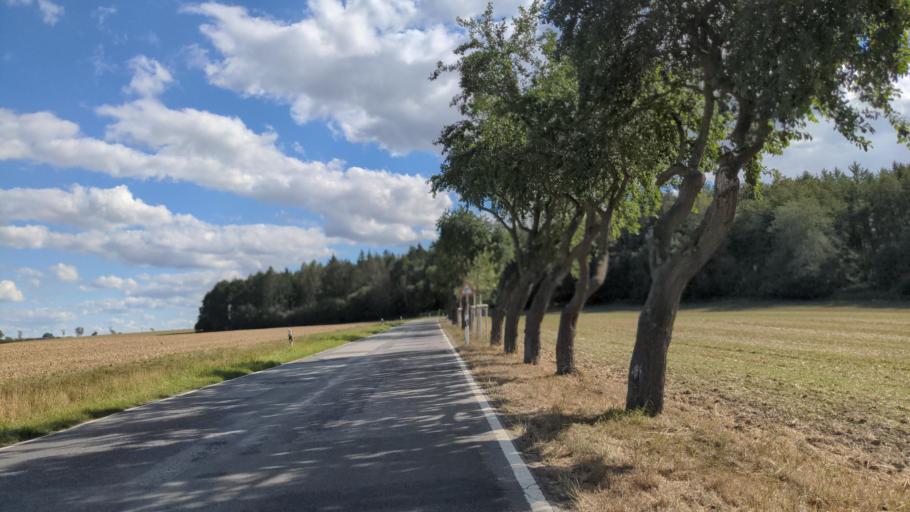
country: DE
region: Mecklenburg-Vorpommern
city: Gramkow
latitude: 53.9175
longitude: 11.3750
